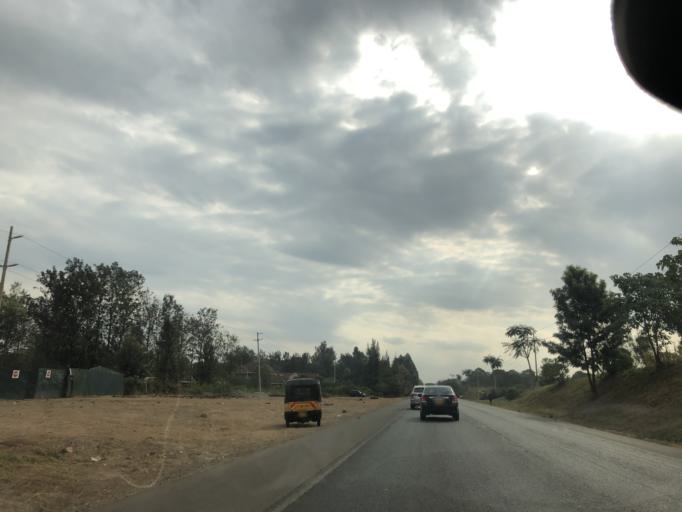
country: KE
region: Kiambu
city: Kiambu
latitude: -1.2152
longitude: 36.8615
